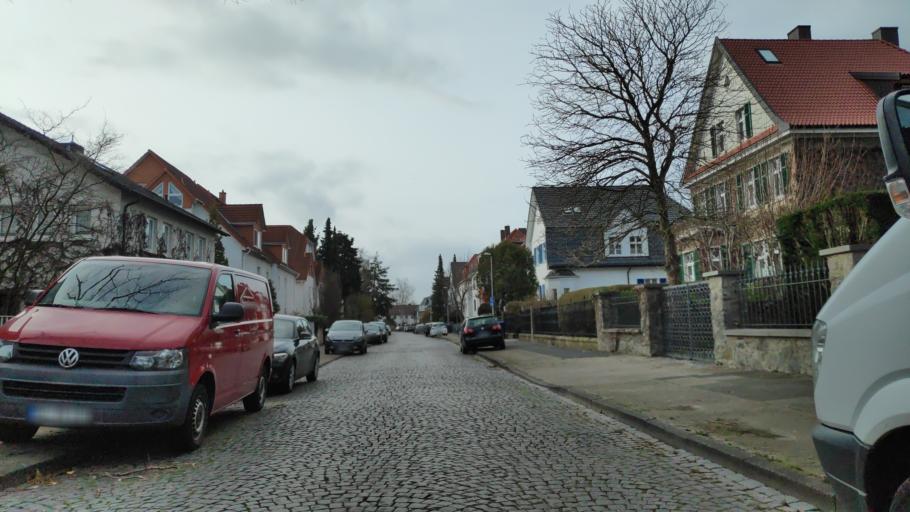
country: DE
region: North Rhine-Westphalia
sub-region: Regierungsbezirk Detmold
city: Minden
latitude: 52.2946
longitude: 8.9072
